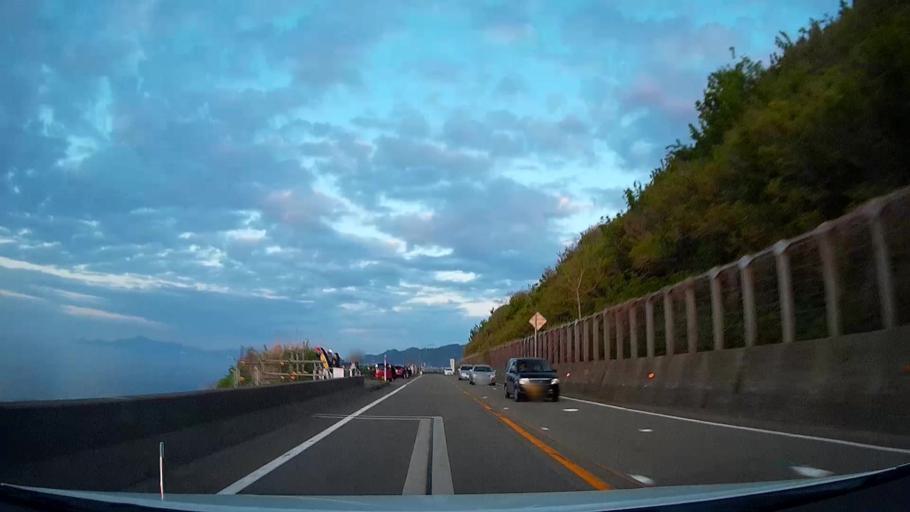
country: JP
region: Niigata
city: Joetsu
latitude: 37.1704
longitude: 138.1200
